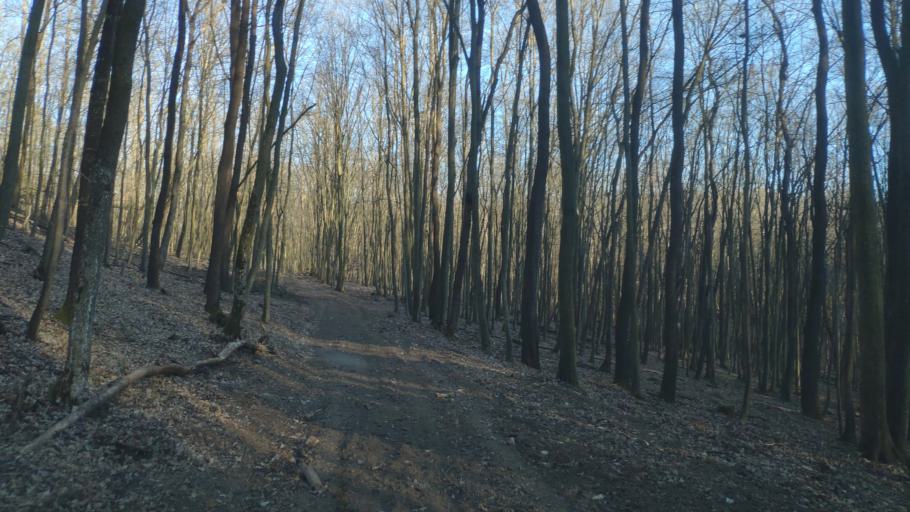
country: HU
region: Borsod-Abauj-Zemplen
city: Putnok
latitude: 48.5040
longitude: 20.3181
